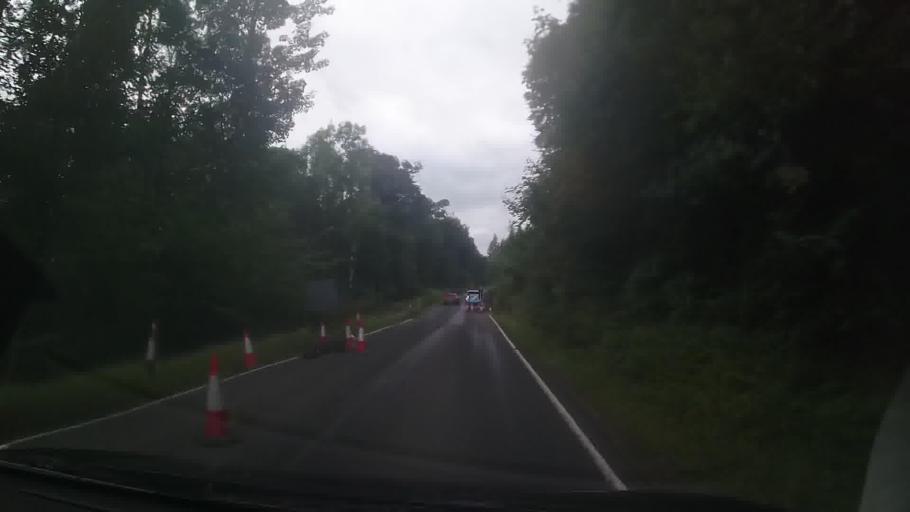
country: GB
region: Scotland
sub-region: Argyll and Bute
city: Garelochhead
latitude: 56.2360
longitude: -5.0792
